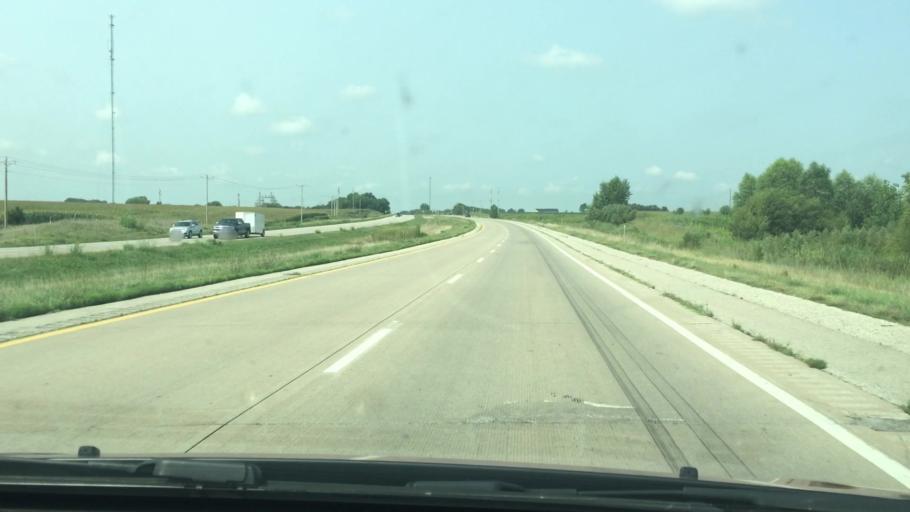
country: US
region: Iowa
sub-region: Cedar County
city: Durant
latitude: 41.5199
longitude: -90.8744
